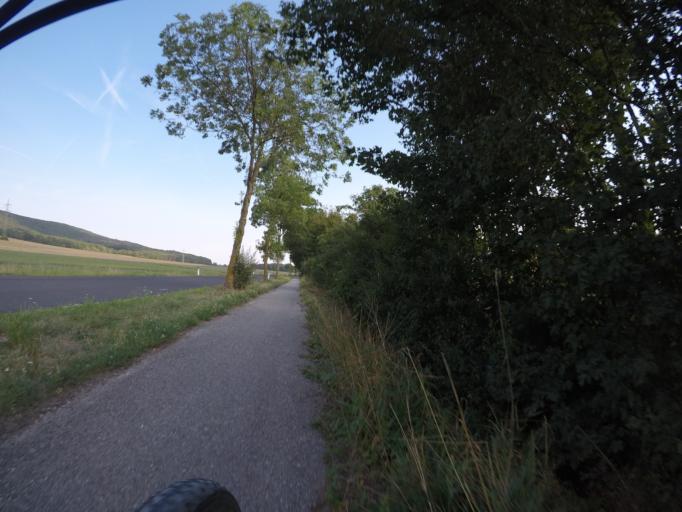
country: AT
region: Lower Austria
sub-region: Politischer Bezirk Baden
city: Berndorf
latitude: 47.9675
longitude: 16.1485
